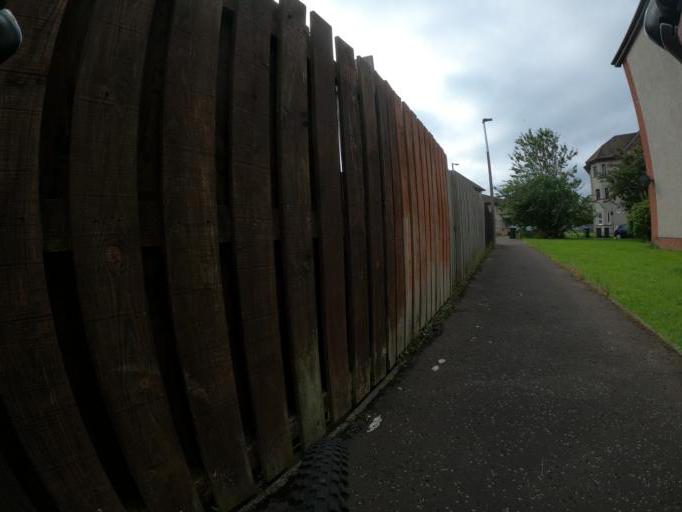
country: GB
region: Scotland
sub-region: Edinburgh
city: Edinburgh
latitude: 55.9733
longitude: -3.2473
